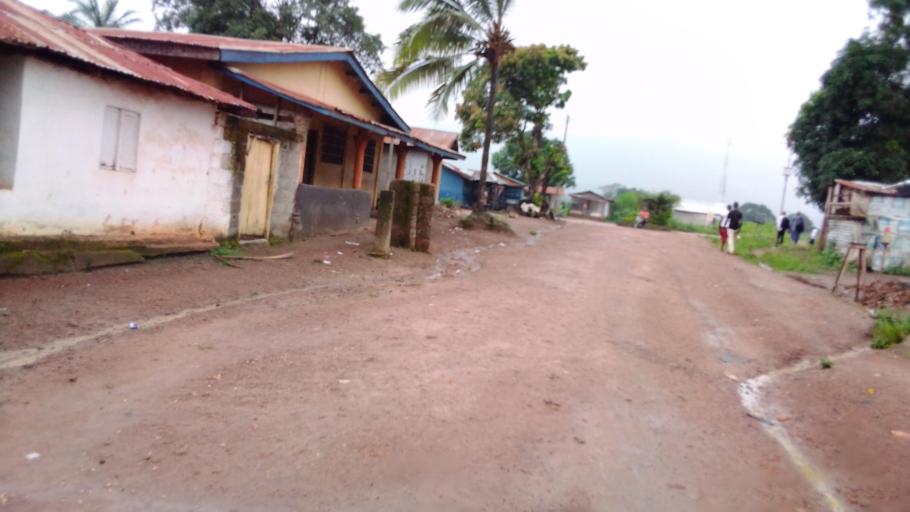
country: SL
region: Eastern Province
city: Kenema
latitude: 7.8957
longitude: -11.1727
